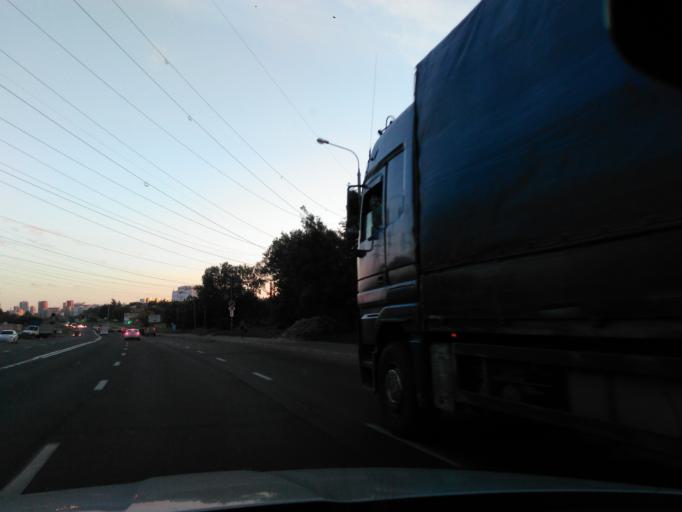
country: RU
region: Moscow
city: Businovo
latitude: 55.8880
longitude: 37.5095
